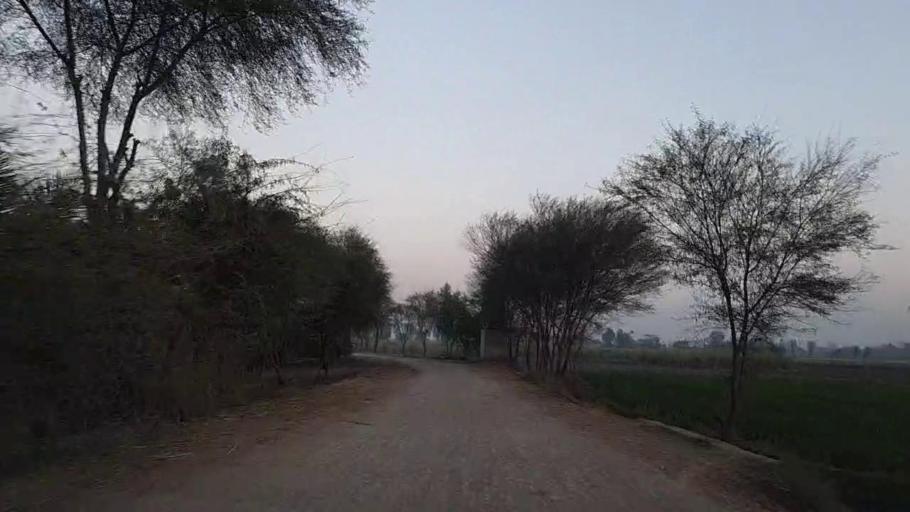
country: PK
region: Sindh
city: Naushahro Firoz
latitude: 26.7905
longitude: 68.0432
